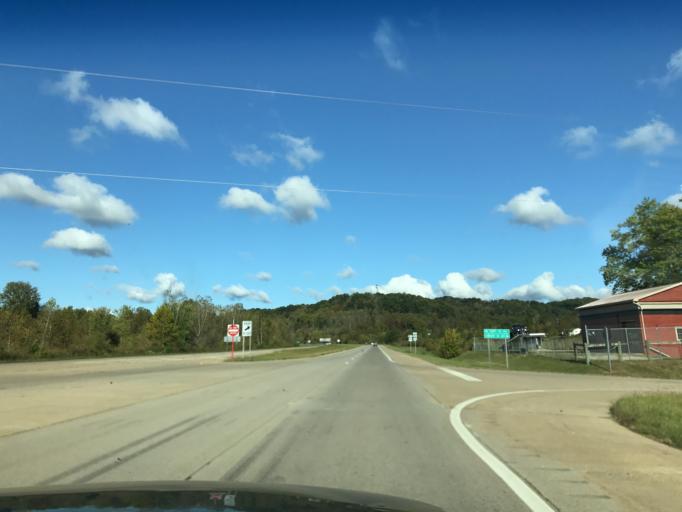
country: US
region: Ohio
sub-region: Athens County
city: Athens
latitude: 39.3297
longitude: -82.0024
